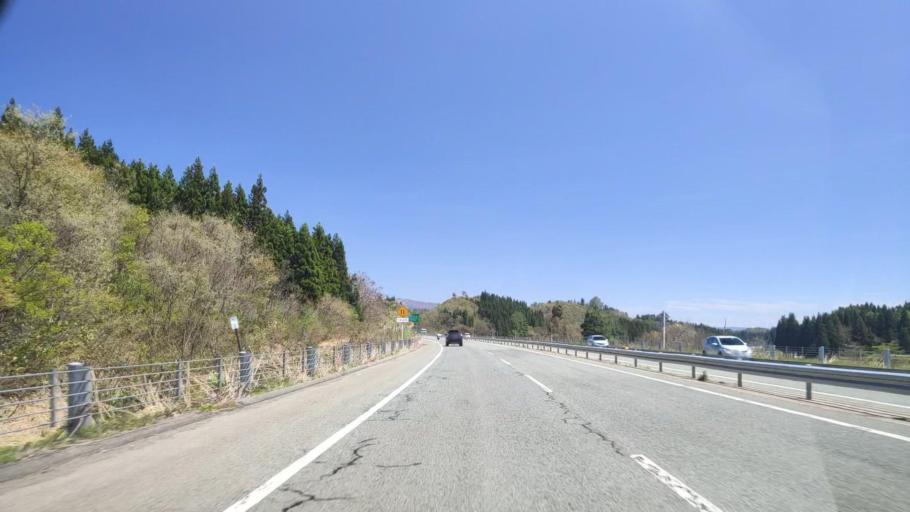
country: JP
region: Yamagata
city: Obanazawa
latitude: 38.6671
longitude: 140.3387
